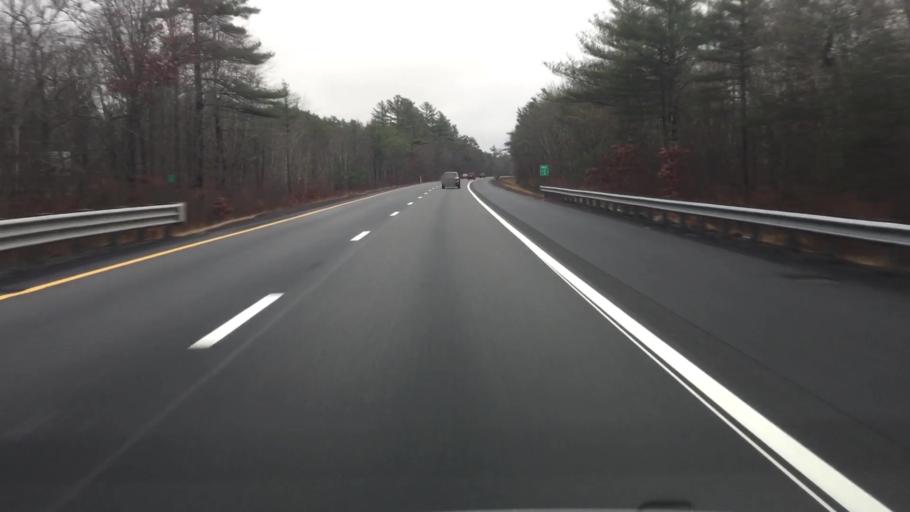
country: US
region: Massachusetts
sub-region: Plymouth County
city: Carver
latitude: 41.8402
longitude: -70.8292
